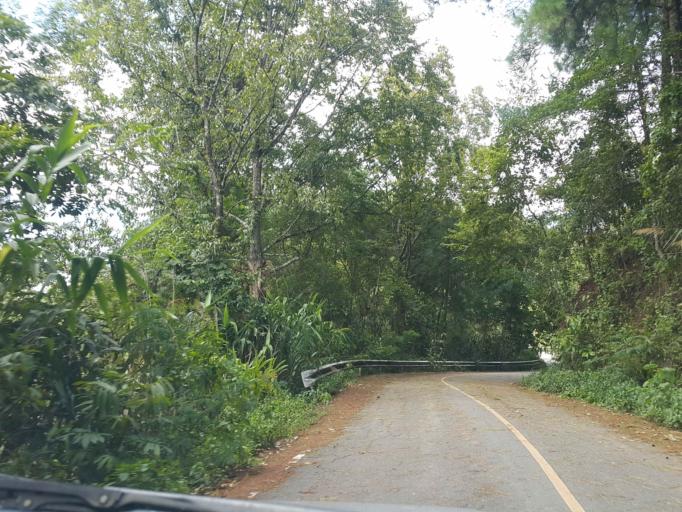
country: TH
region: Chiang Mai
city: Mae Chaem
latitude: 18.5180
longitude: 98.5212
